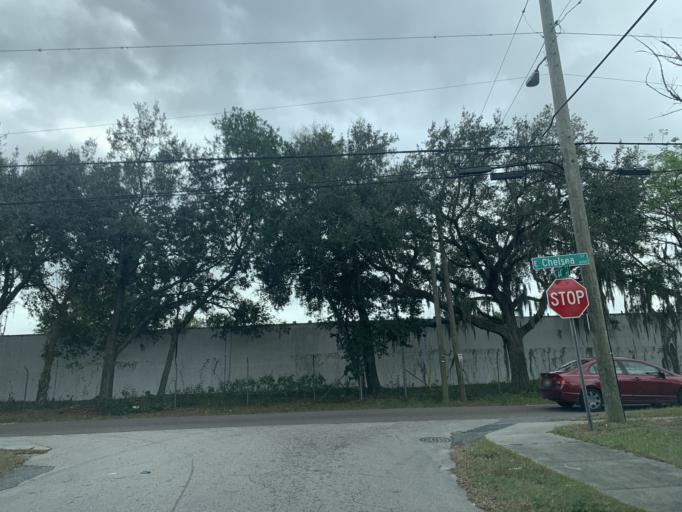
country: US
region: Florida
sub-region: Hillsborough County
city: East Lake-Orient Park
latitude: 27.9854
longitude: -82.4085
